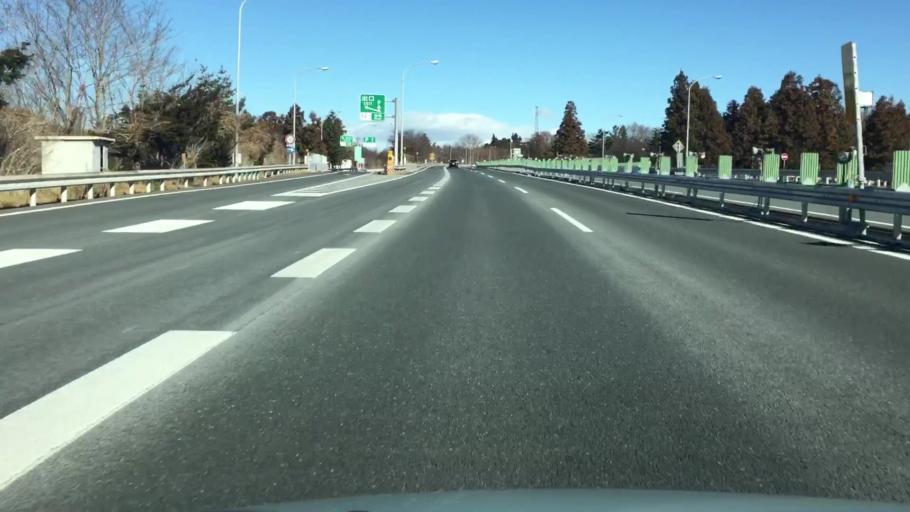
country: JP
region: Gunma
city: Shibukawa
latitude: 36.5355
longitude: 139.0477
